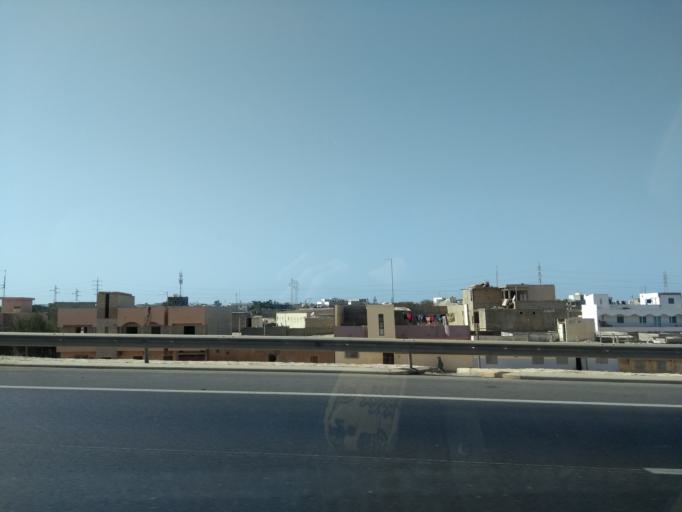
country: SN
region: Dakar
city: Pikine
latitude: 14.7447
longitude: -17.3937
